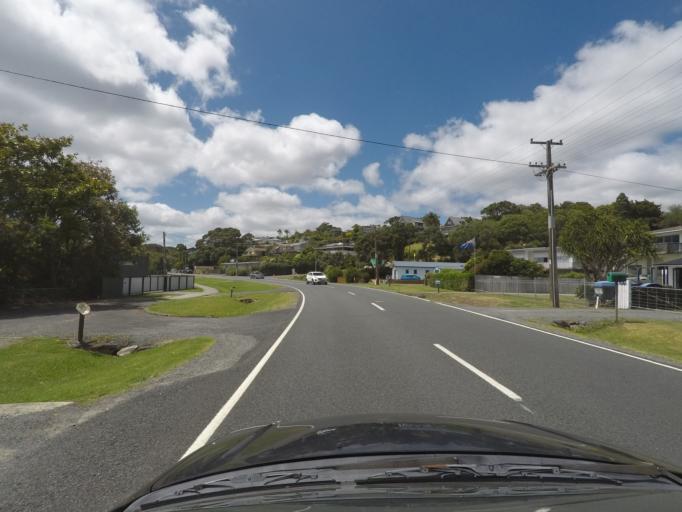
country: NZ
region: Northland
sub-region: Whangarei
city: Ruakaka
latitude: -36.0281
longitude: 174.5029
